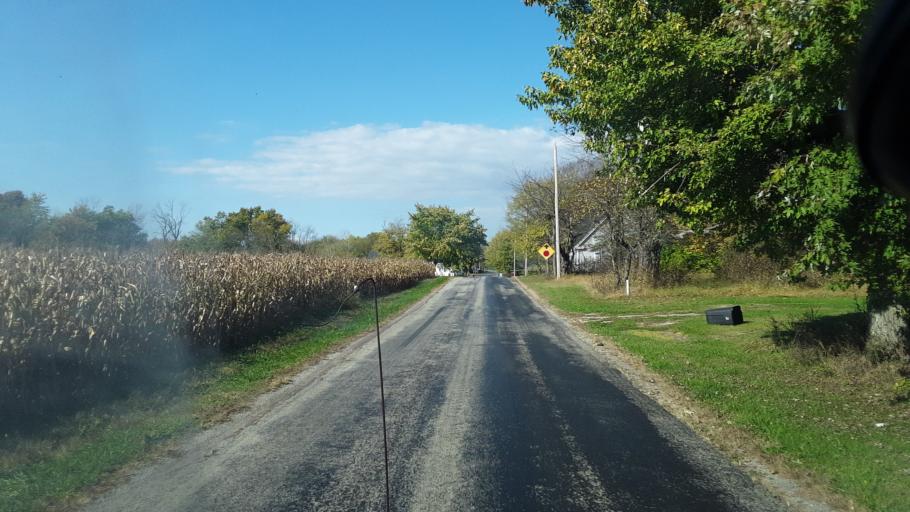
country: US
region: Ohio
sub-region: Highland County
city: Leesburg
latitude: 39.2831
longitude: -83.5894
